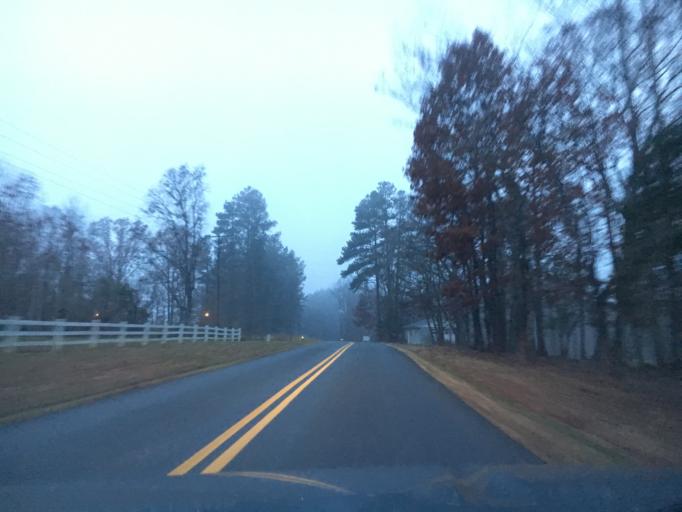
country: US
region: Virginia
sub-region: Halifax County
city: Mountain Road
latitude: 36.6836
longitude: -79.0024
